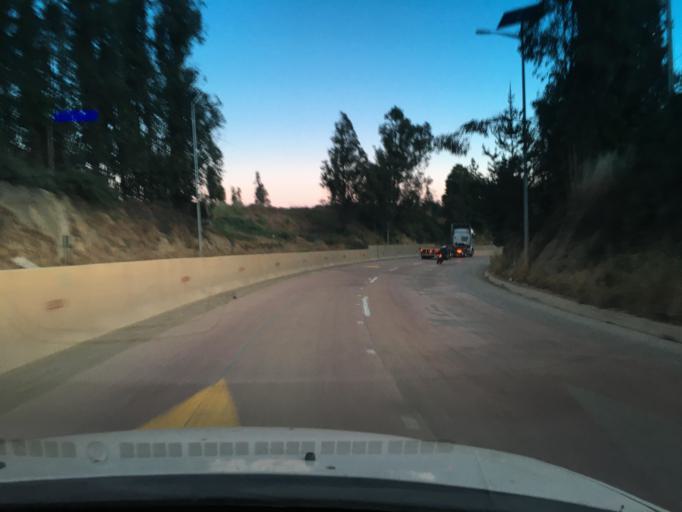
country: CL
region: Valparaiso
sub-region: Provincia de Valparaiso
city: Vina del Mar
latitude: -33.0988
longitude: -71.5735
